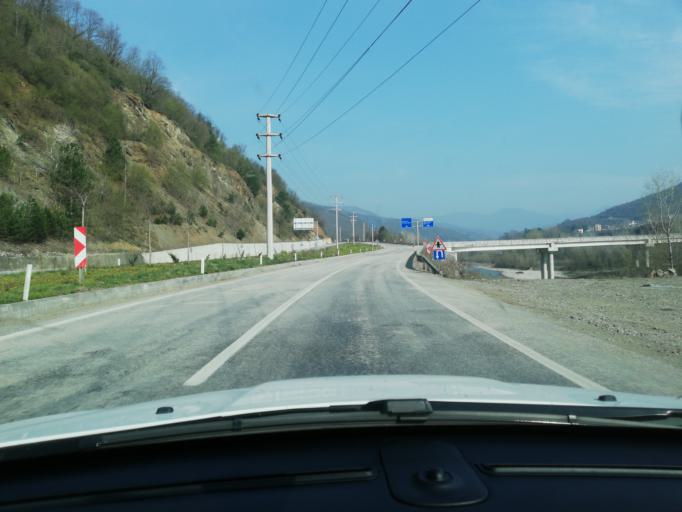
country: TR
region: Karabuk
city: Yenice
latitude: 41.2051
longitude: 32.3660
